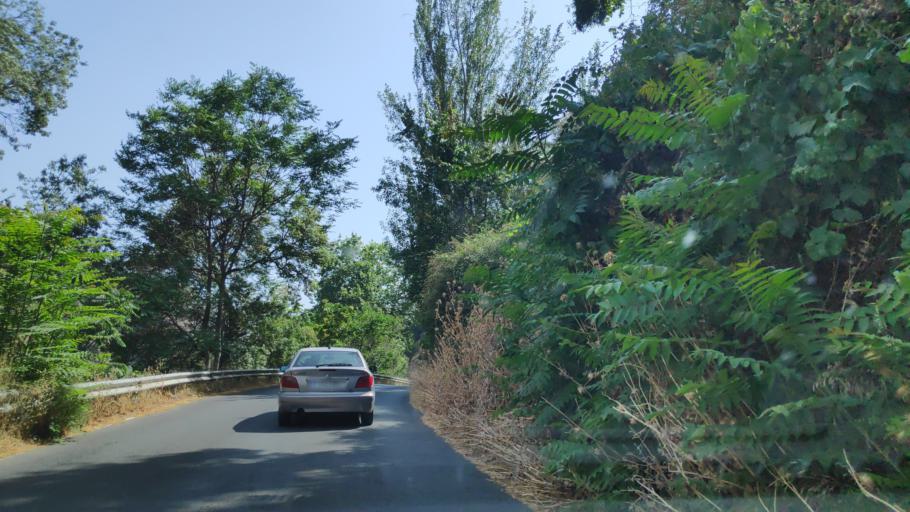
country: ES
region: Andalusia
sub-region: Provincia de Granada
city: Pampaneira
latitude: 36.9395
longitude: -3.3653
